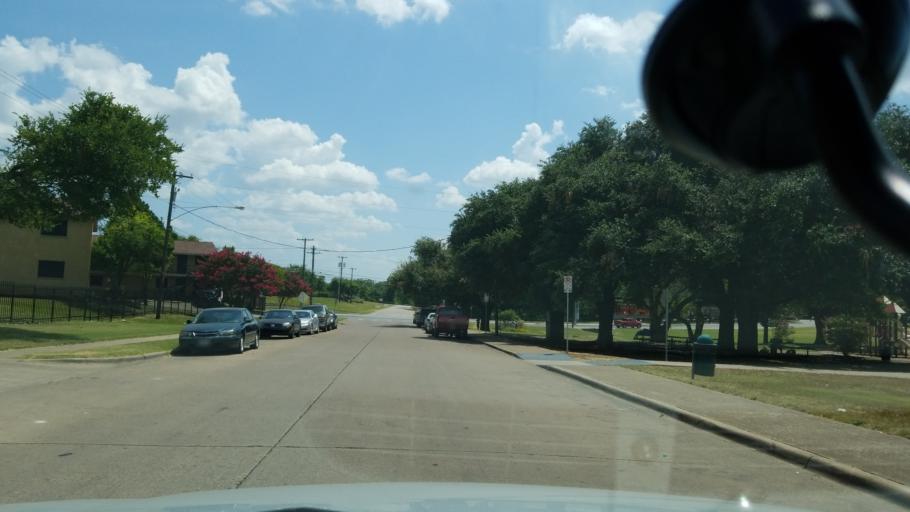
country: US
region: Texas
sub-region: Dallas County
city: Cockrell Hill
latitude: 32.7214
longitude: -96.8785
